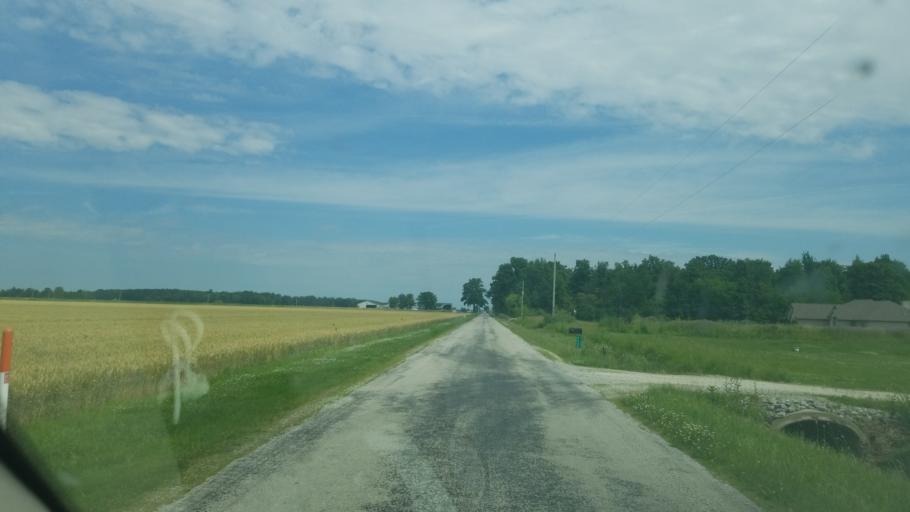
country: US
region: Ohio
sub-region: Wood County
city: North Baltimore
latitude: 41.2047
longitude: -83.5733
